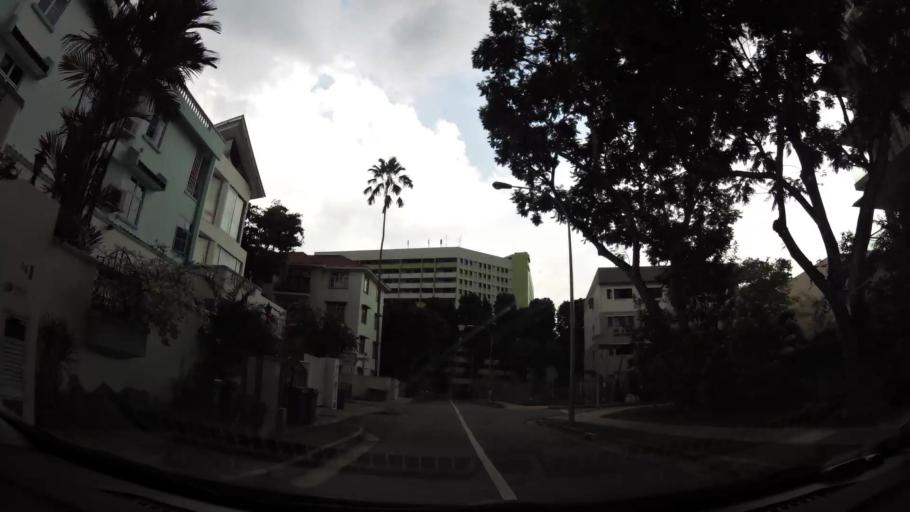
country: SG
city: Singapore
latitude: 1.3135
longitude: 103.8492
